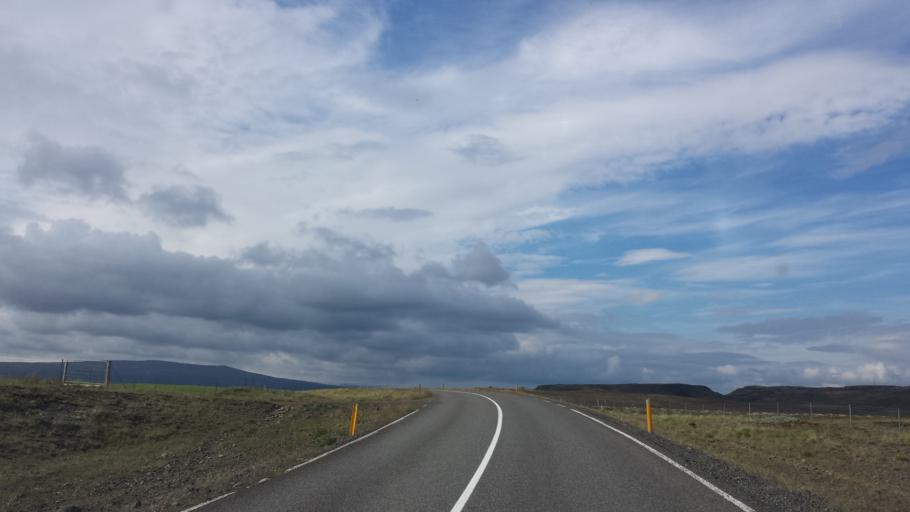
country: IS
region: South
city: Vestmannaeyjar
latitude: 64.2648
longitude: -20.2233
